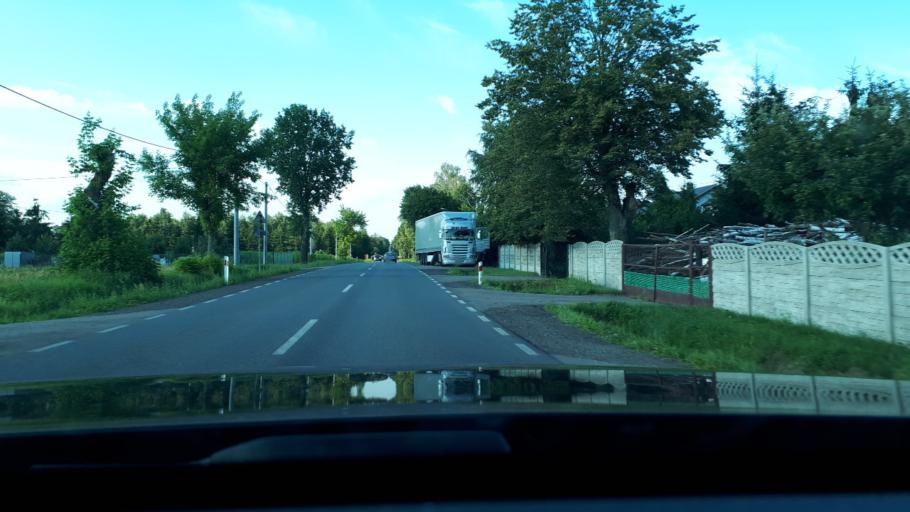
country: PL
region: Masovian Voivodeship
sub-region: Powiat ciechanowski
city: Ojrzen
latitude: 52.7471
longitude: 20.5291
